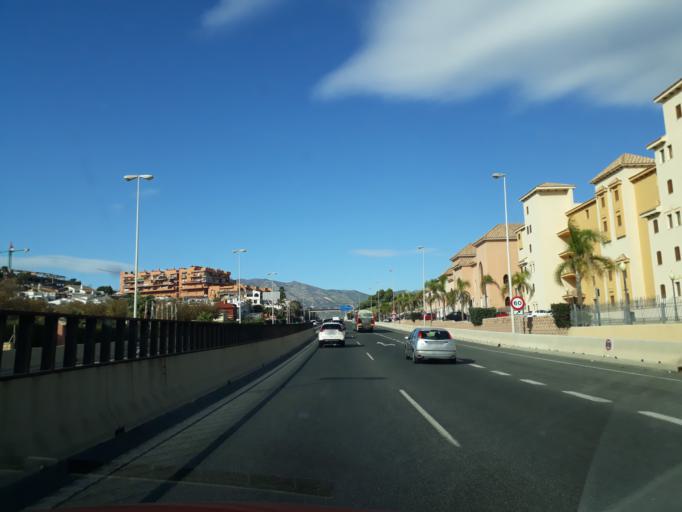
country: ES
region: Andalusia
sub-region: Provincia de Malaga
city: Fuengirola
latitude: 36.5205
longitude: -4.6301
